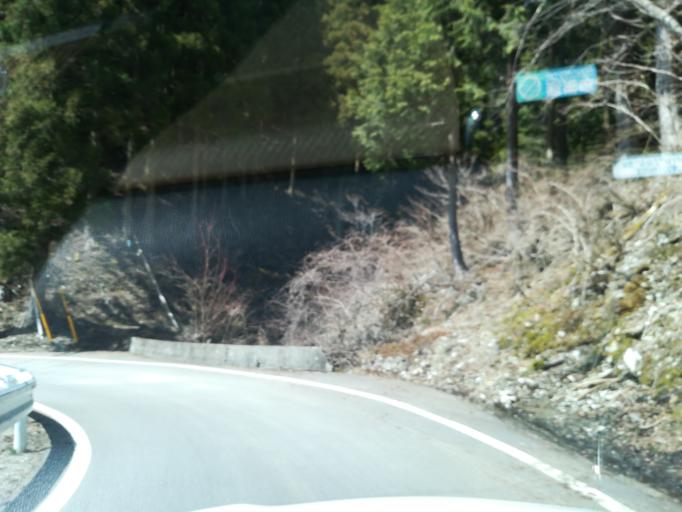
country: JP
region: Tokushima
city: Wakimachi
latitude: 33.8663
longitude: 134.0724
